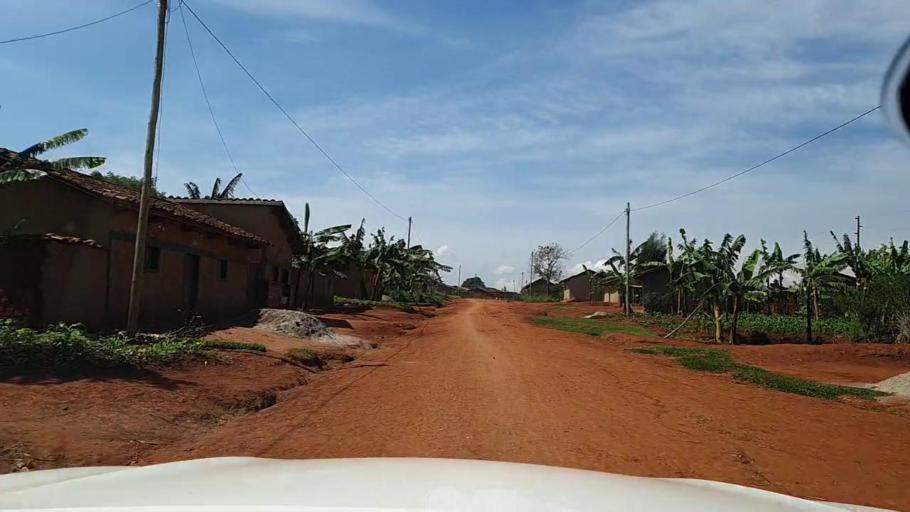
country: RW
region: Southern Province
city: Butare
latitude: -2.7190
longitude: 29.8382
